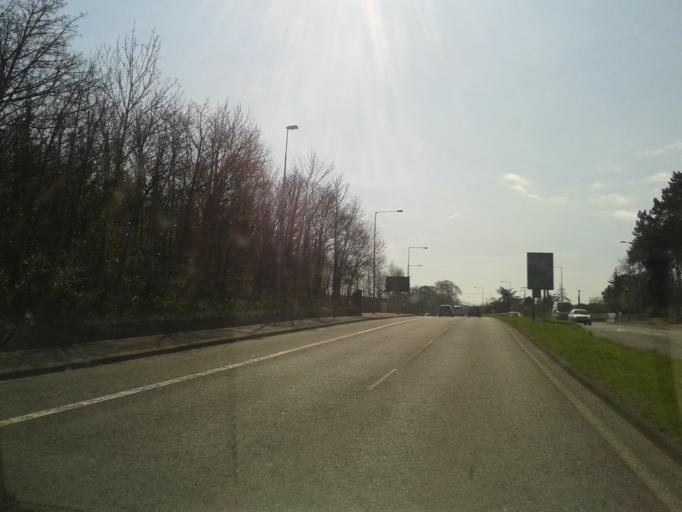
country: IE
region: Leinster
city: Loughlinstown
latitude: 53.2567
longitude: -6.1456
